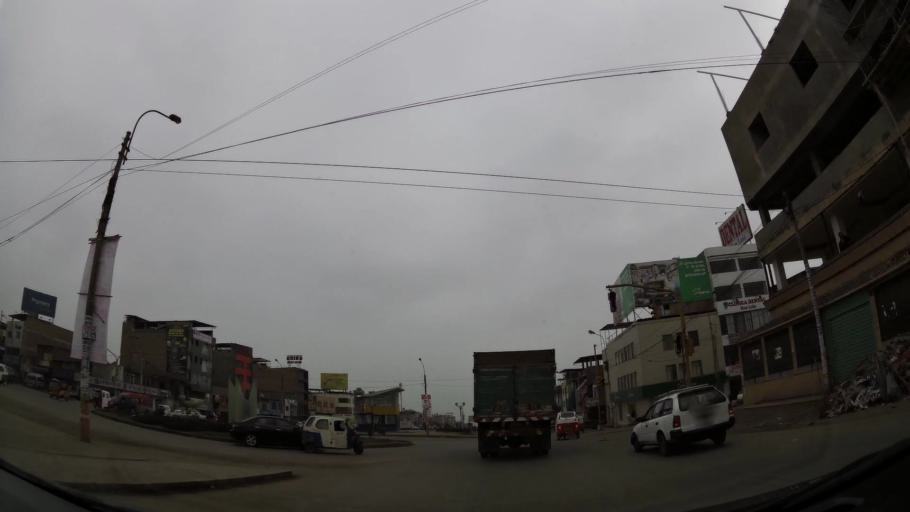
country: PE
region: Lima
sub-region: Lima
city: Surco
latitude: -12.2065
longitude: -76.9373
